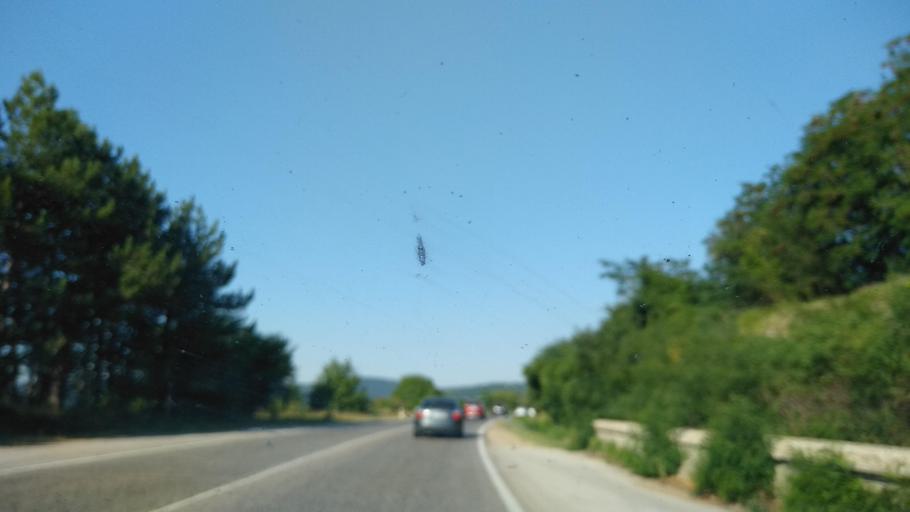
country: BG
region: Lovech
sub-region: Obshtina Lovech
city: Lovech
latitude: 43.0441
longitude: 24.8518
